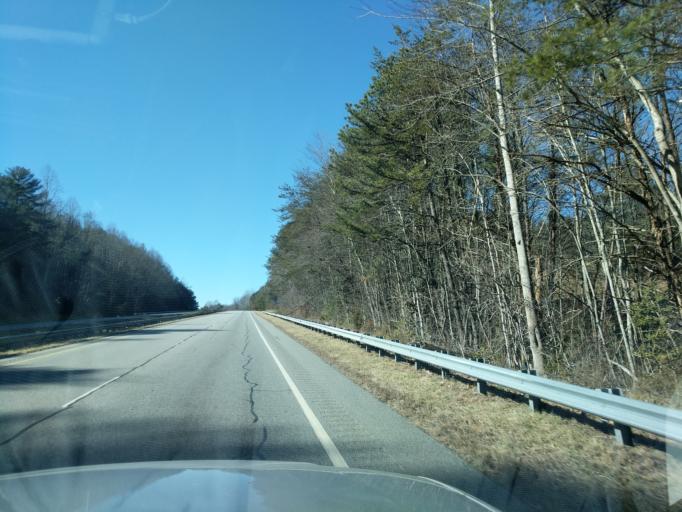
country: US
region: North Carolina
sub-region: Swain County
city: Bryson City
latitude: 35.4252
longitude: -83.4276
